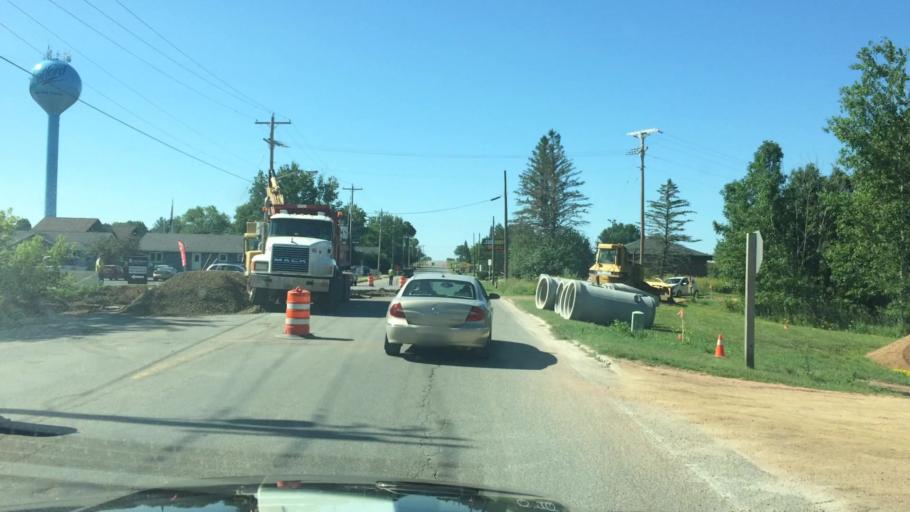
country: US
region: Wisconsin
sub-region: Marathon County
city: Stratford
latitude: 44.7982
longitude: -90.0792
